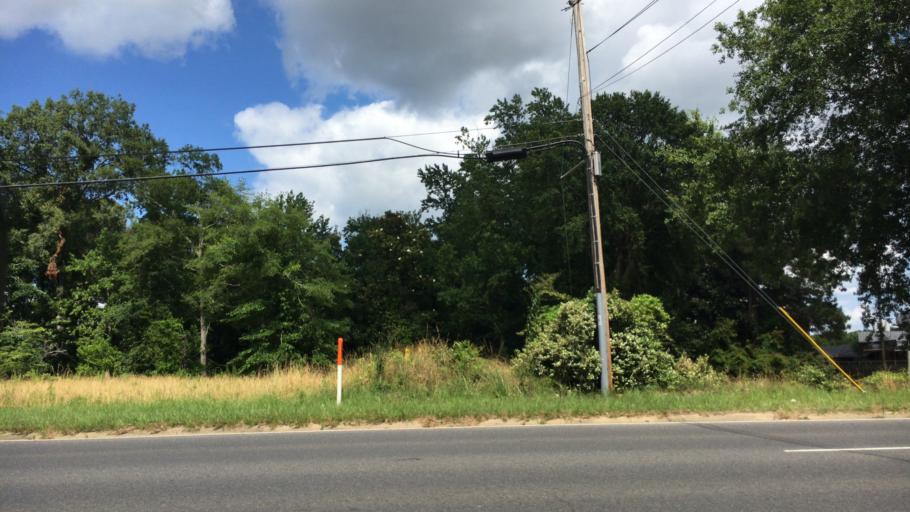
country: US
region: Louisiana
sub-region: Lincoln Parish
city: Ruston
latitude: 32.5462
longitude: -92.6397
